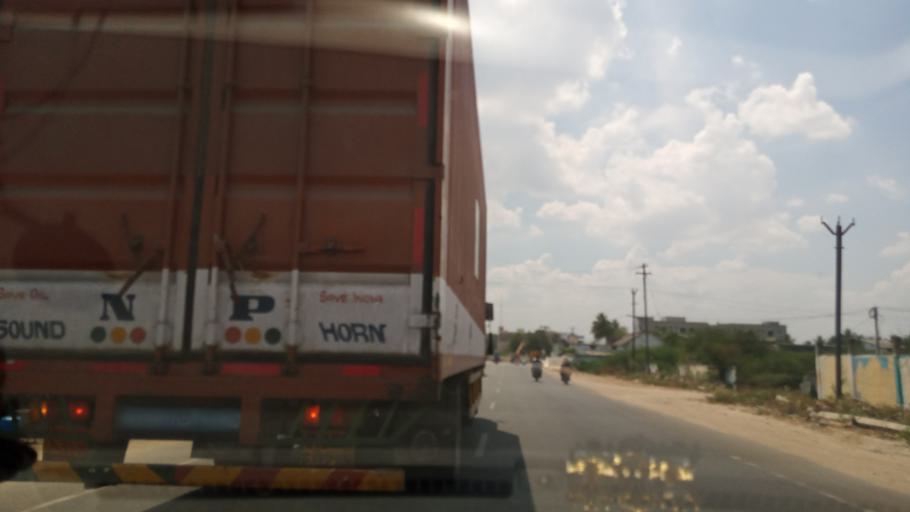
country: IN
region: Tamil Nadu
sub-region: Vellore
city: Walajapet
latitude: 12.9301
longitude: 79.3395
